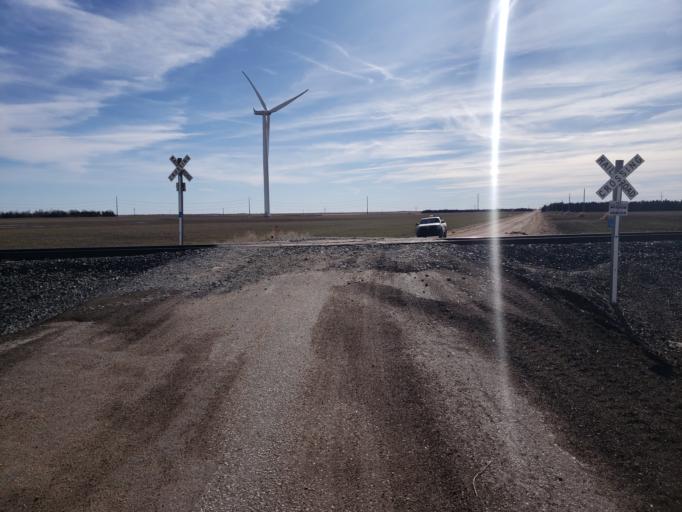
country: US
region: Kansas
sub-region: Ford County
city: Dodge City
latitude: 37.8127
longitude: -99.8328
